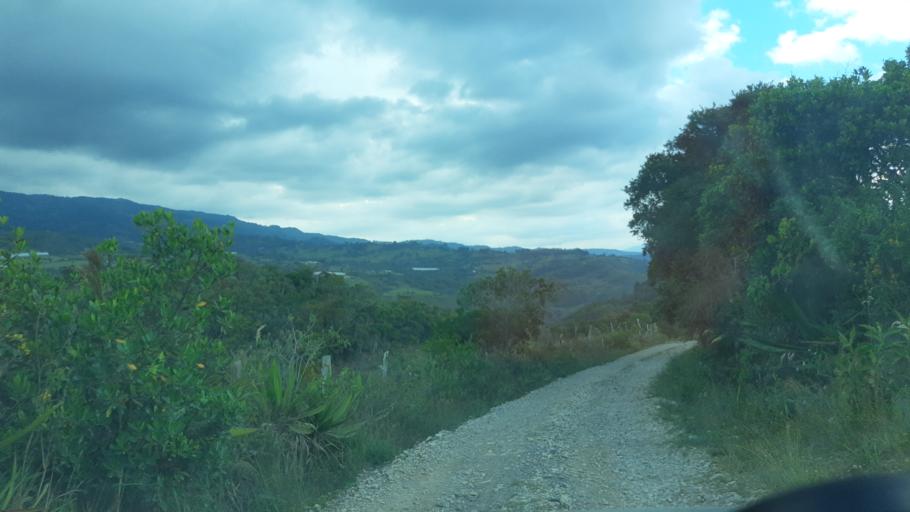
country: CO
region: Boyaca
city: Santa Sofia
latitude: 5.7483
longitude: -73.5747
